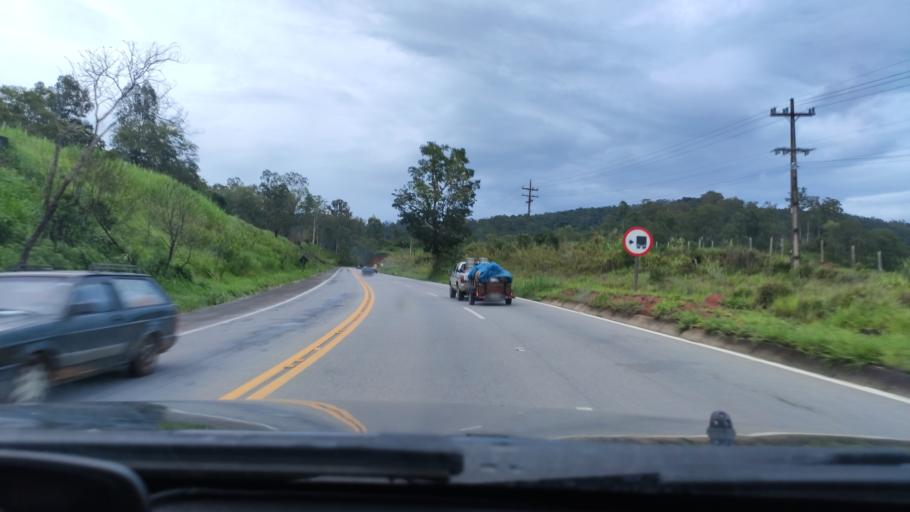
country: BR
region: Sao Paulo
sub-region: Braganca Paulista
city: Braganca Paulista
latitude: -22.8380
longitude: -46.5524
